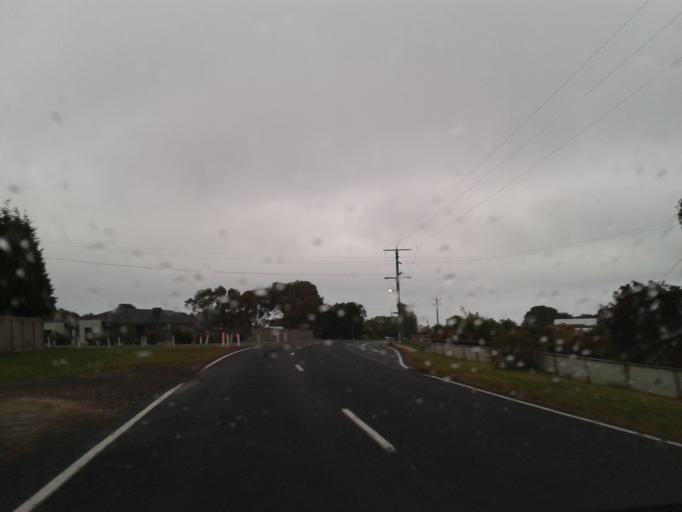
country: AU
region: Victoria
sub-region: Glenelg
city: Portland
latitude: -38.3407
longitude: 141.5722
